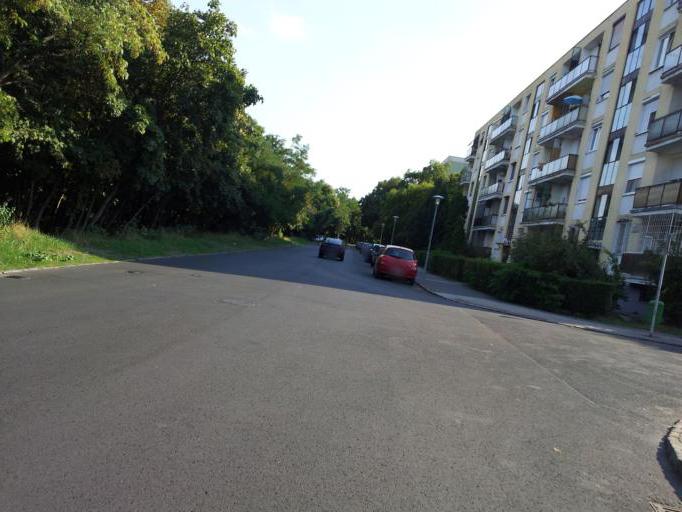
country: HU
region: Budapest
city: Budapest XIX. keruelet
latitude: 47.4628
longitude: 19.1194
